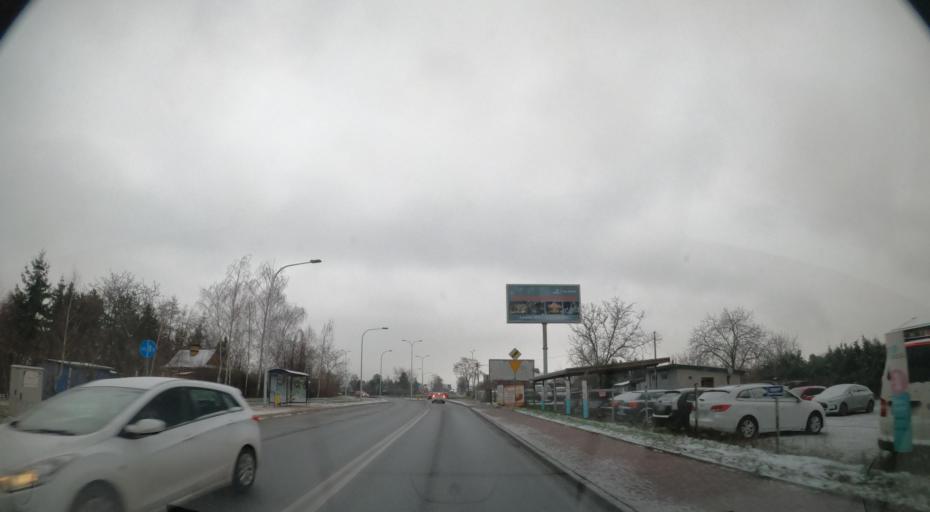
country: PL
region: Masovian Voivodeship
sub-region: Powiat plocki
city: Maszewo Duze
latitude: 52.5644
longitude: 19.6575
